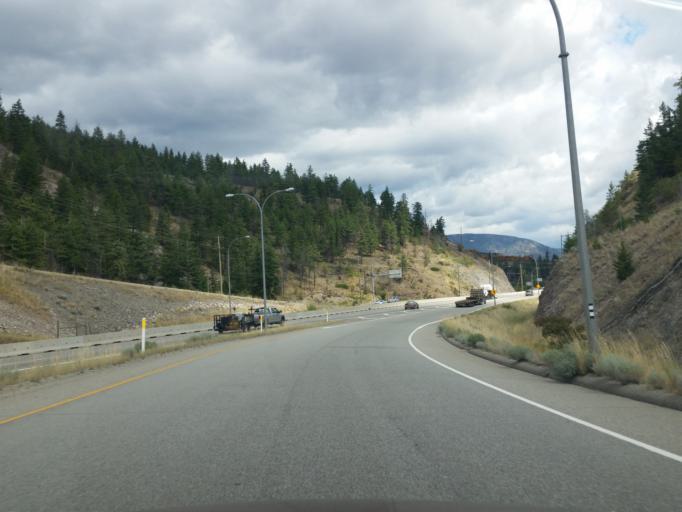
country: CA
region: British Columbia
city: Peachland
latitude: 49.8084
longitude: -119.6615
